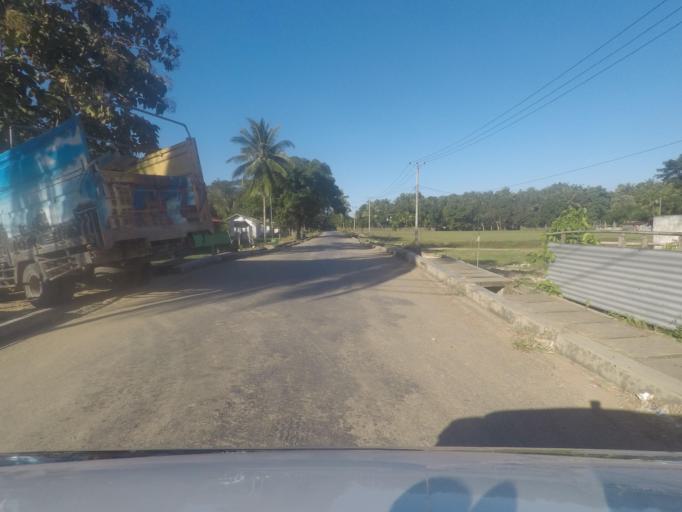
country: TL
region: Lautem
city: Lospalos
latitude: -8.3997
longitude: 127.1860
